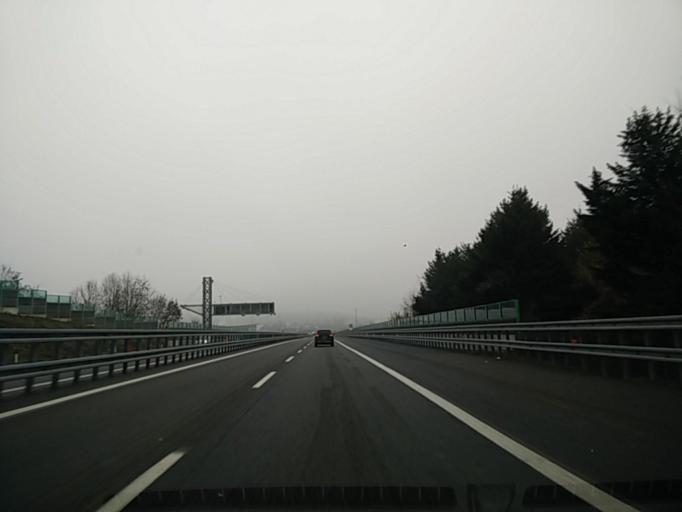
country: IT
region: Piedmont
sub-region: Provincia di Asti
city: Asti
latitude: 44.9149
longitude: 8.2164
